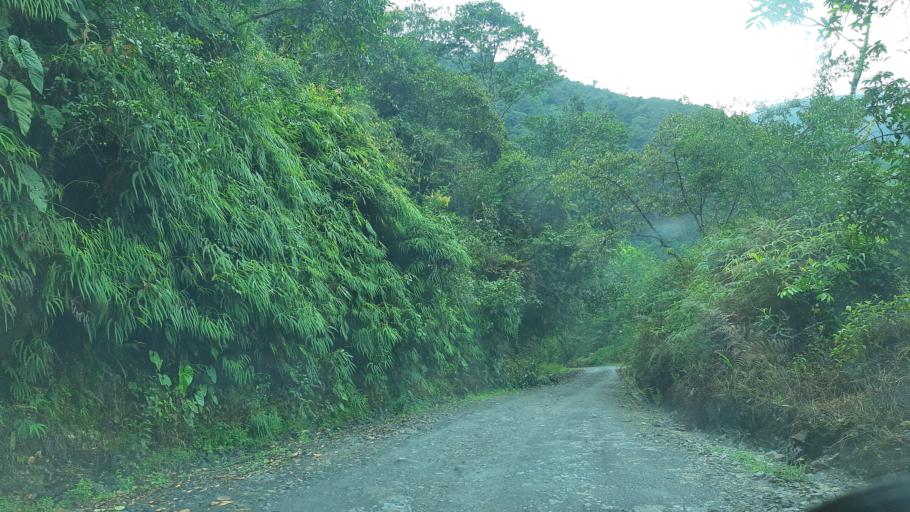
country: CO
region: Boyaca
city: Chivor
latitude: 4.9122
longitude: -73.3071
